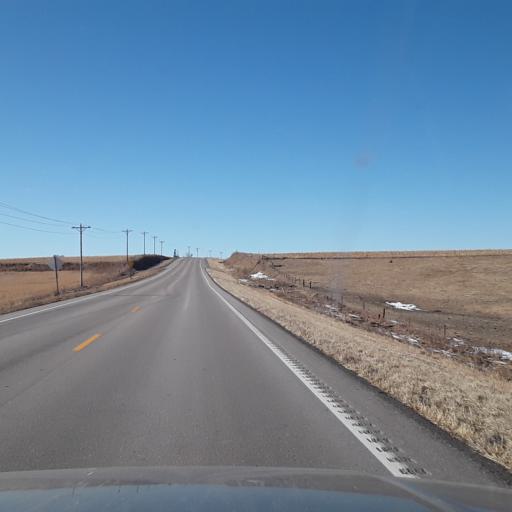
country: US
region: Nebraska
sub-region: Dawson County
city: Gothenburg
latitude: 40.7039
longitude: -100.1926
